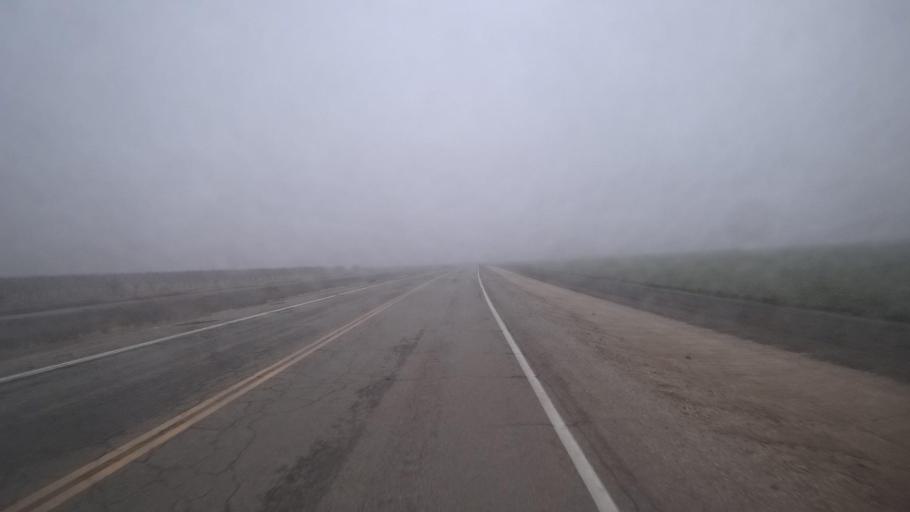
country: US
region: California
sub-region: Kern County
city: Buttonwillow
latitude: 35.4325
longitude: -119.5428
